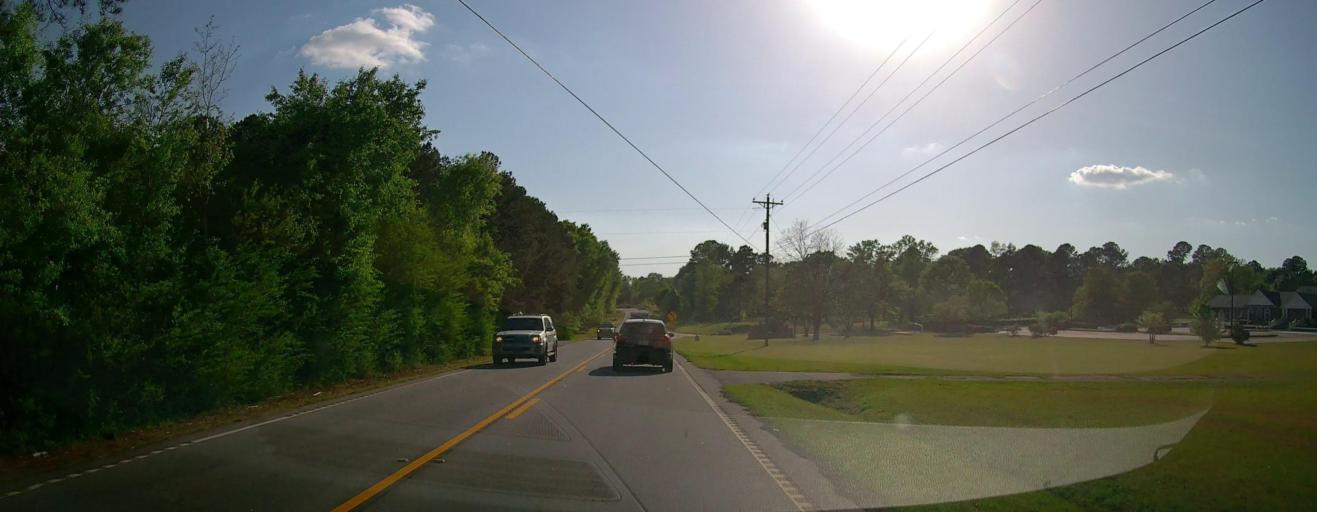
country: US
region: Georgia
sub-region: Walton County
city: Social Circle
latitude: 33.6230
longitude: -83.6834
